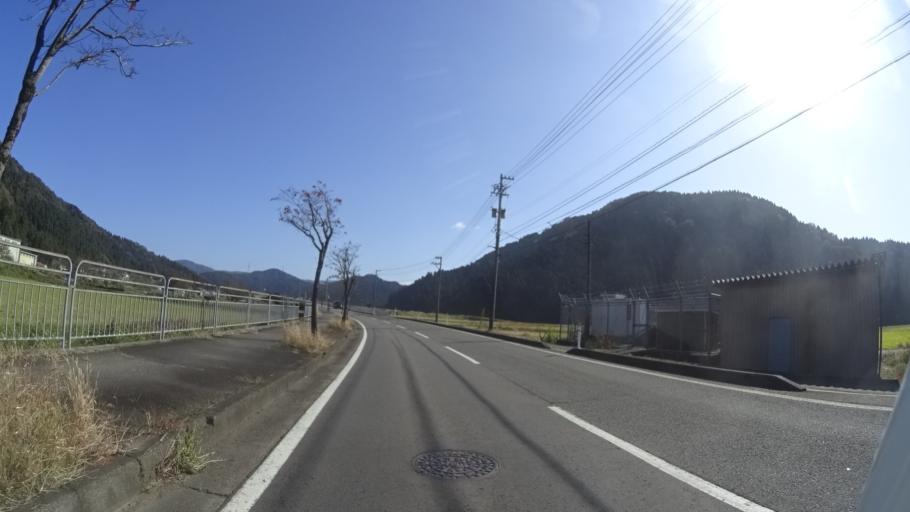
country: JP
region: Fukui
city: Sabae
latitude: 35.9484
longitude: 136.2508
